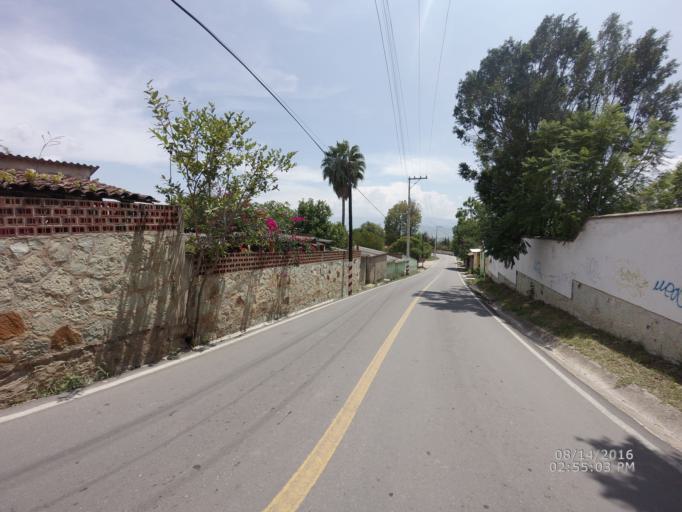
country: MX
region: Oaxaca
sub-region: San Juan Bautista Guelache
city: Fraccionamiento San Miguel
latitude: 17.1965
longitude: -96.7642
